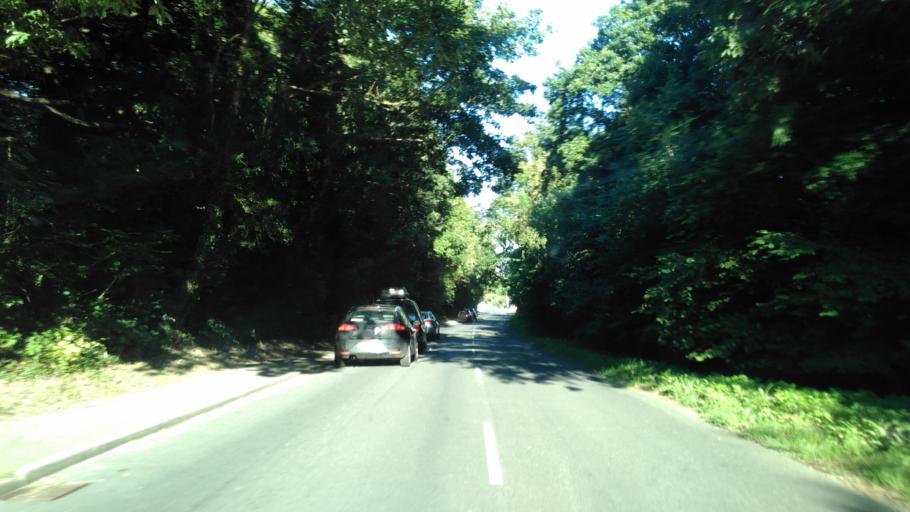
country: GB
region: England
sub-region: Kent
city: Dunkirk
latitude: 51.2912
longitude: 0.9837
